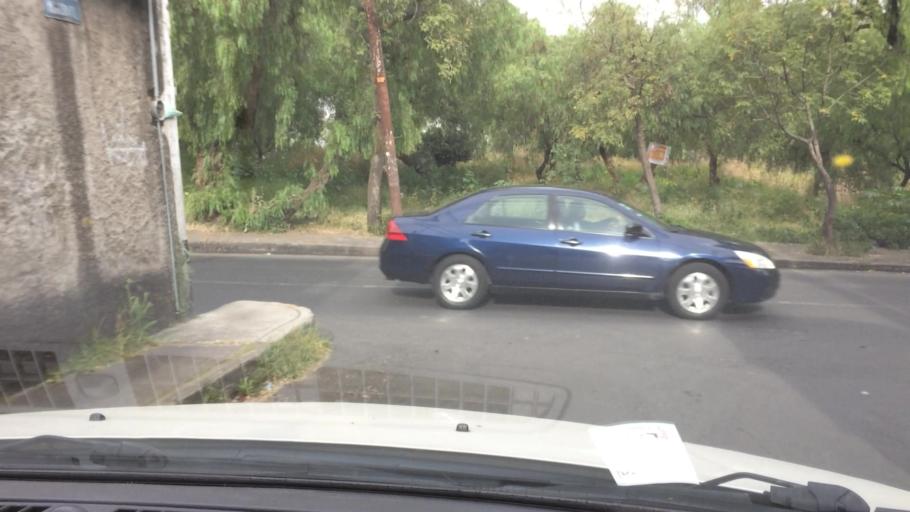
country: MX
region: Mexico City
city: Xochimilco
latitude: 19.2673
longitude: -99.1280
